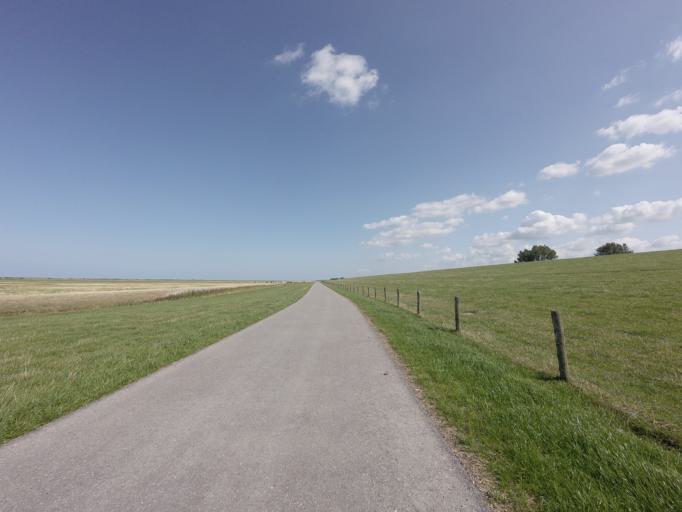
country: NL
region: Friesland
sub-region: Gemeente Ferwerderadiel
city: Marrum
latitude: 53.3415
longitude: 5.7905
